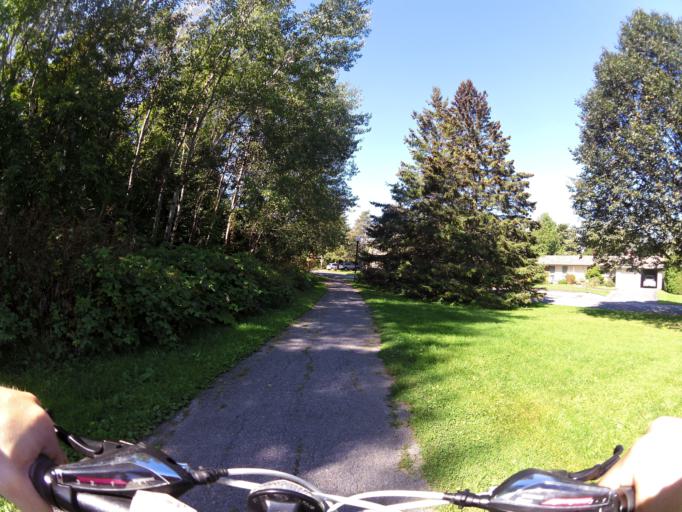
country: CA
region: Ontario
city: Bells Corners
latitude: 45.3238
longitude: -75.8988
